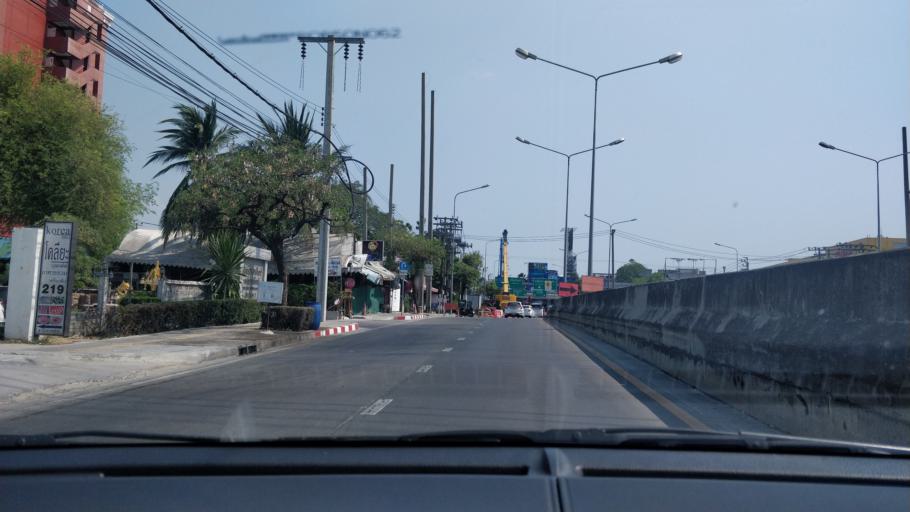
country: TH
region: Bangkok
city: Watthana
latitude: 13.7391
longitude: 100.6164
